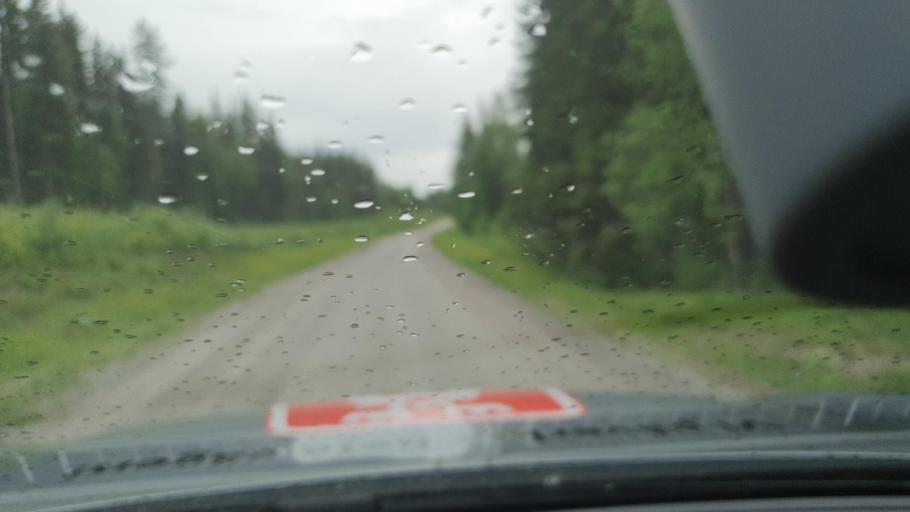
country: SE
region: Norrbotten
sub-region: Kalix Kommun
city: Rolfs
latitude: 66.0360
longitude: 23.0627
